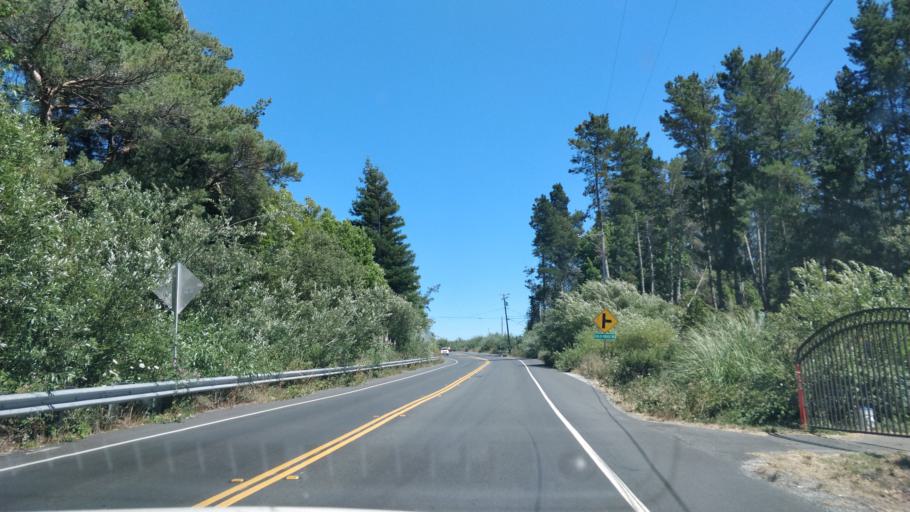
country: US
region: California
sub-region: Sonoma County
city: Graton
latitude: 38.3950
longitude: -122.8658
